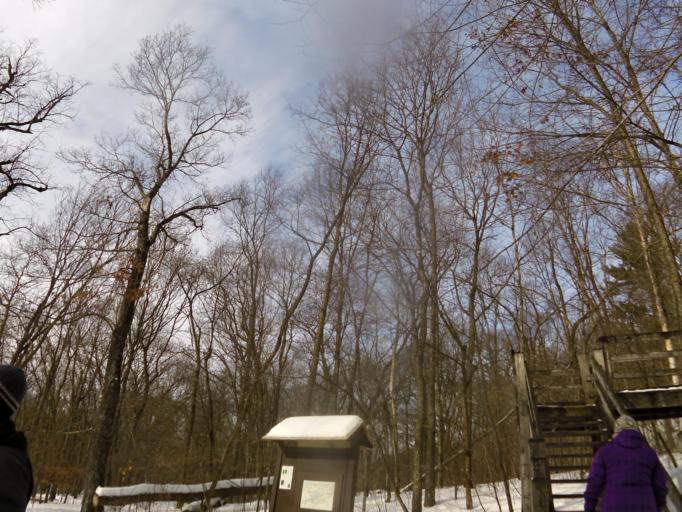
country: US
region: Wisconsin
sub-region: Saint Croix County
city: Somerset
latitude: 45.0248
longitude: -92.6603
